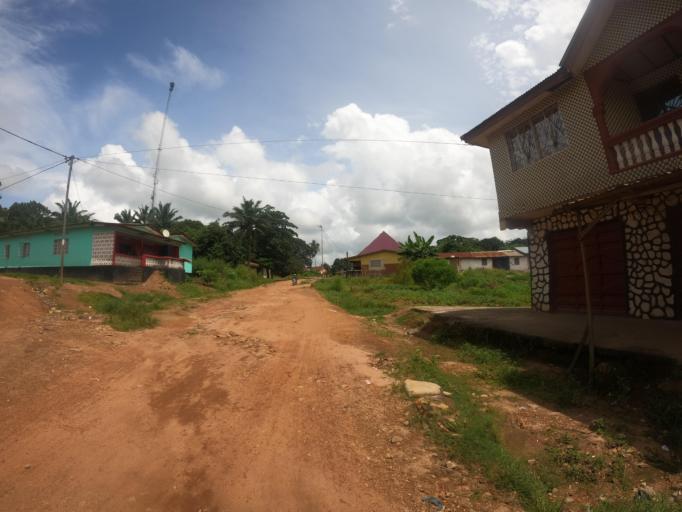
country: SL
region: Northern Province
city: Makeni
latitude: 8.8951
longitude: -12.0569
